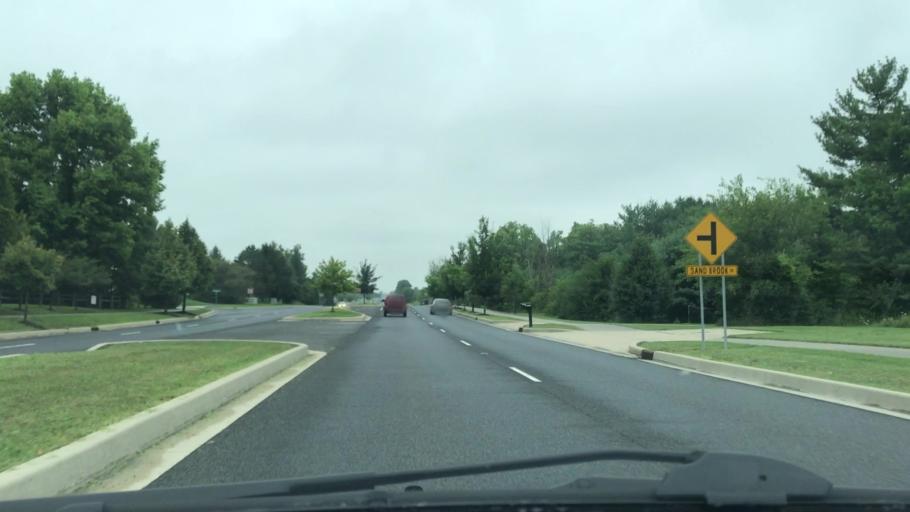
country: US
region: Indiana
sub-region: Hamilton County
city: Westfield
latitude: 40.0503
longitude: -86.0712
